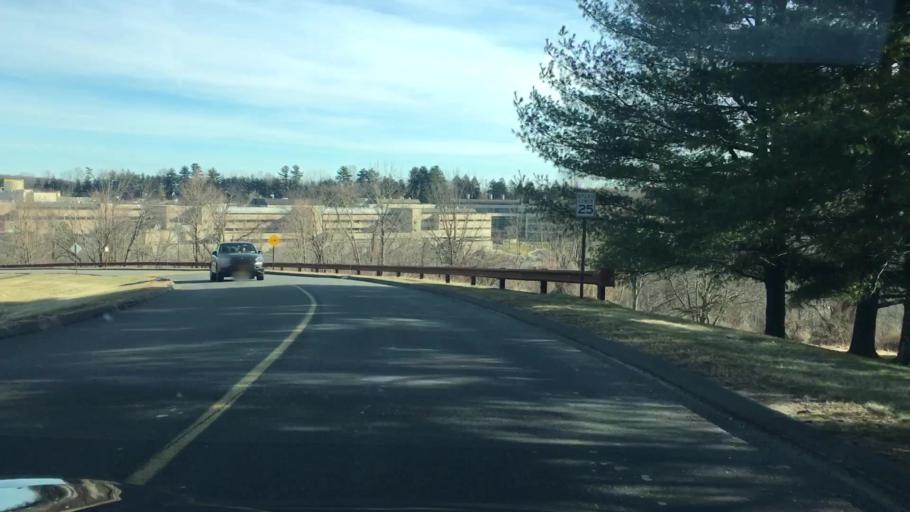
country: US
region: Connecticut
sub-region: Fairfield County
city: Danbury
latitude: 41.3727
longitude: -73.5130
